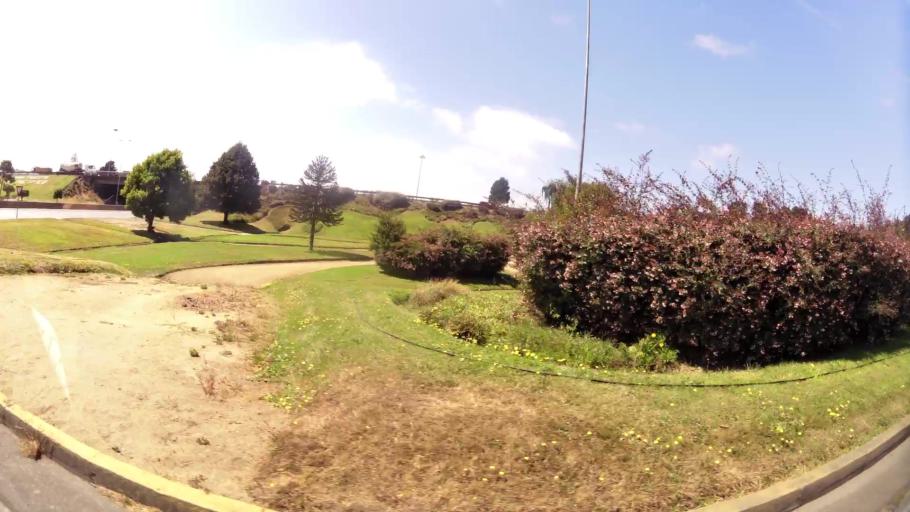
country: CL
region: Biobio
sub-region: Provincia de Concepcion
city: Concepcion
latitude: -36.7964
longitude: -73.0666
